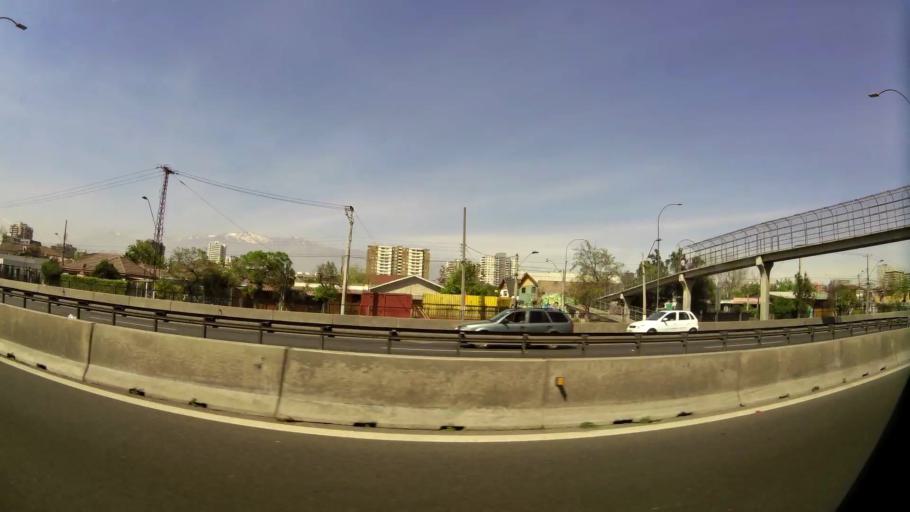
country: CL
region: Santiago Metropolitan
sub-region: Provincia de Santiago
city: Santiago
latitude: -33.4847
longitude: -70.6589
